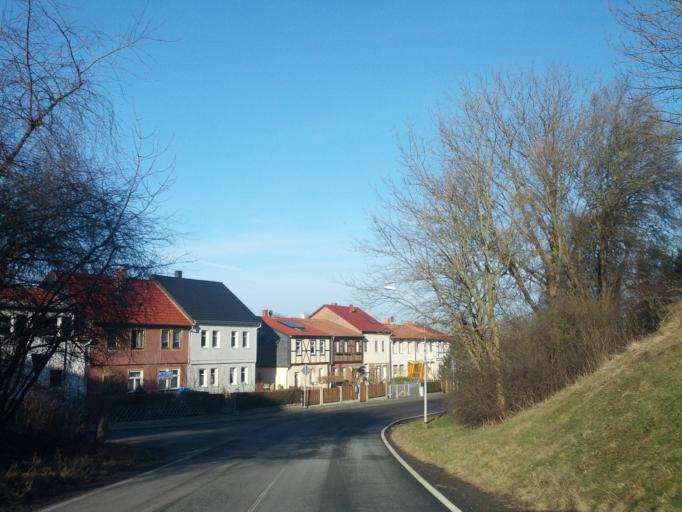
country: DE
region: Thuringia
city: Bad Langensalza
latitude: 51.0990
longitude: 10.6240
